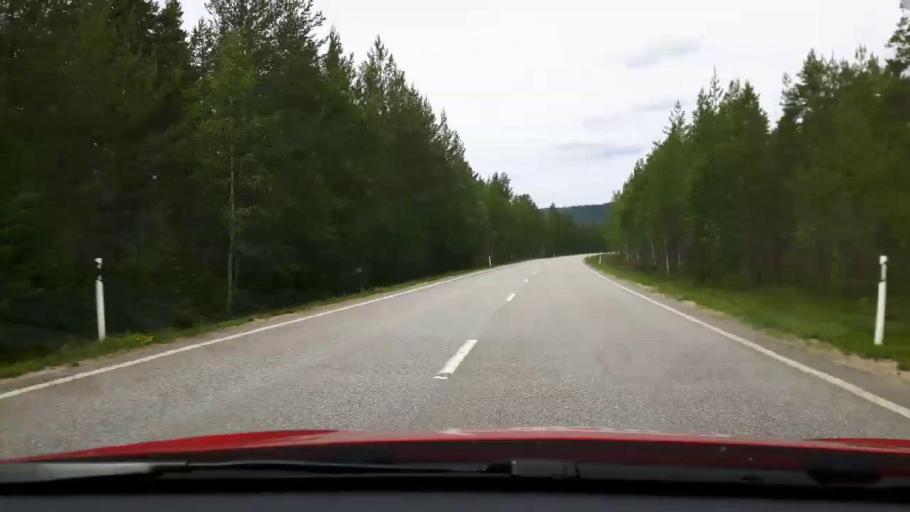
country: SE
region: Jaemtland
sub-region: Harjedalens Kommun
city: Sveg
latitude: 62.0811
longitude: 14.2574
